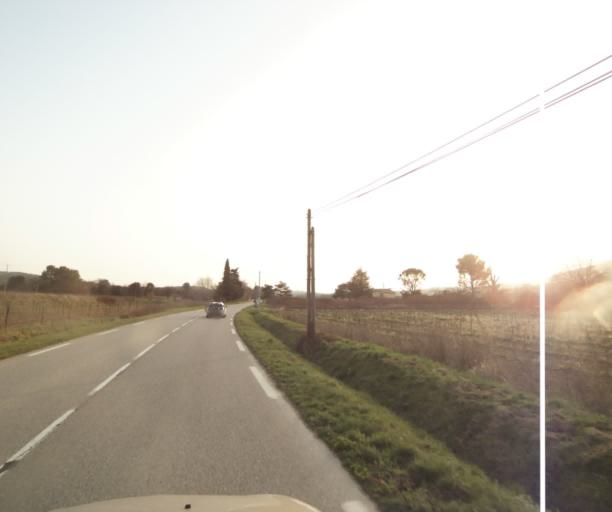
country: FR
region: Provence-Alpes-Cote d'Azur
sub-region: Departement des Bouches-du-Rhone
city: Rognes
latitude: 43.6994
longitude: 5.3473
